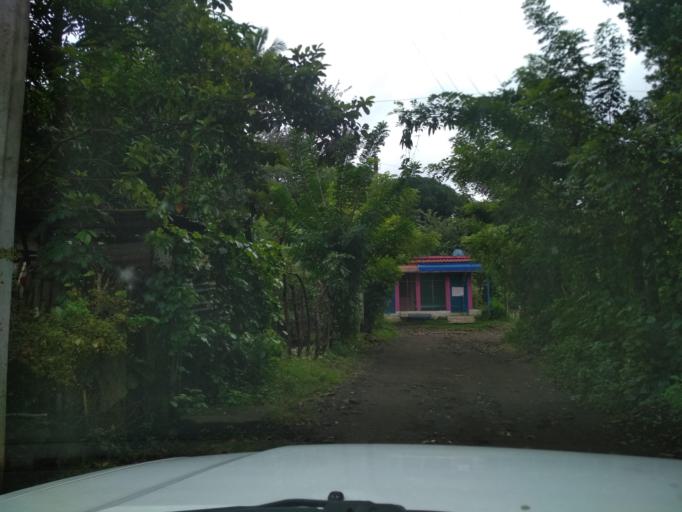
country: MX
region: Veracruz
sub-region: San Andres Tuxtla
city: Matacapan
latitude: 18.4366
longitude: -95.1642
